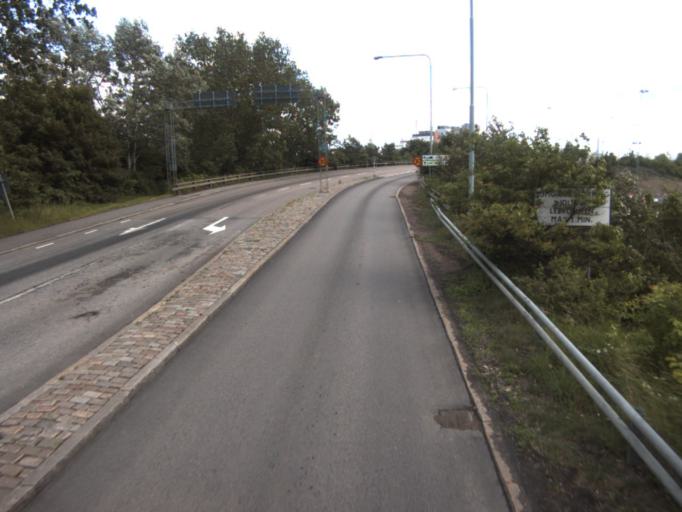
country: SE
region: Skane
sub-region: Helsingborg
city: Helsingborg
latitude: 56.0329
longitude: 12.7000
